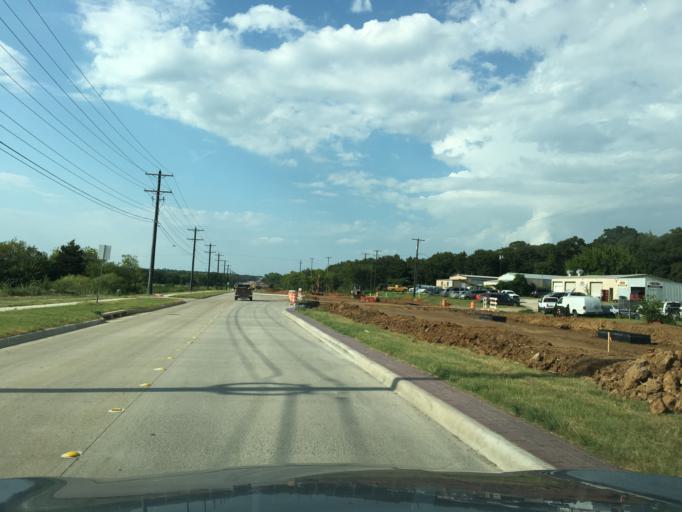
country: US
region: Texas
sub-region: Denton County
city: Denton
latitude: 33.2173
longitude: -97.0836
